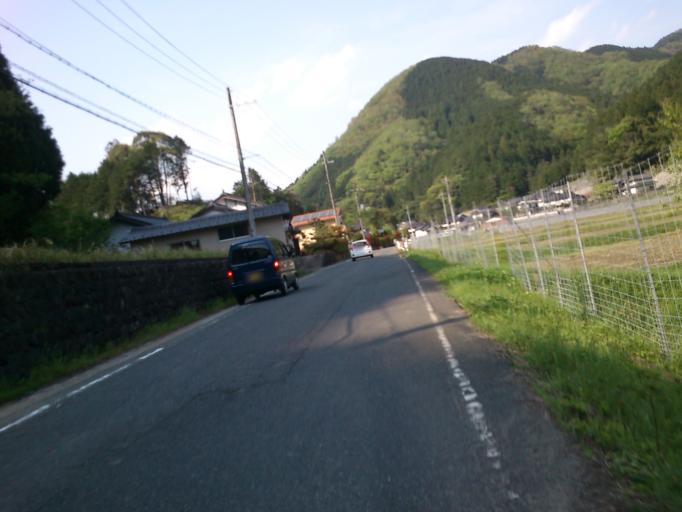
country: JP
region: Kyoto
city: Fukuchiyama
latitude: 35.3274
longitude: 135.0054
